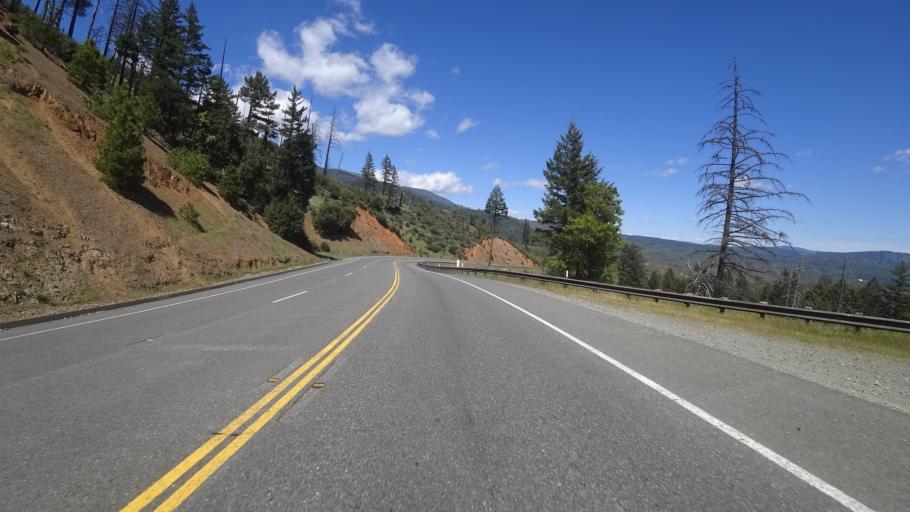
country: US
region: California
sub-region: Trinity County
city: Weaverville
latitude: 40.7399
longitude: -122.9805
